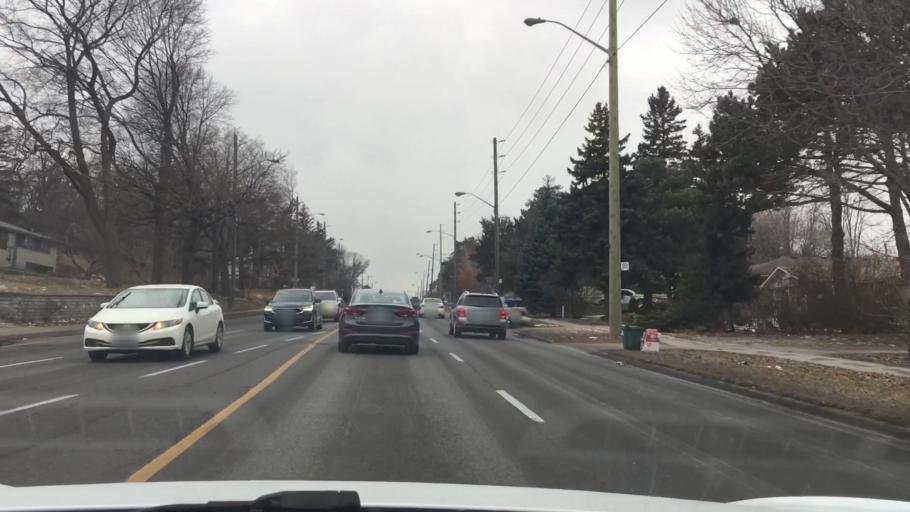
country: CA
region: Ontario
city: Willowdale
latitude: 43.8010
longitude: -79.4068
